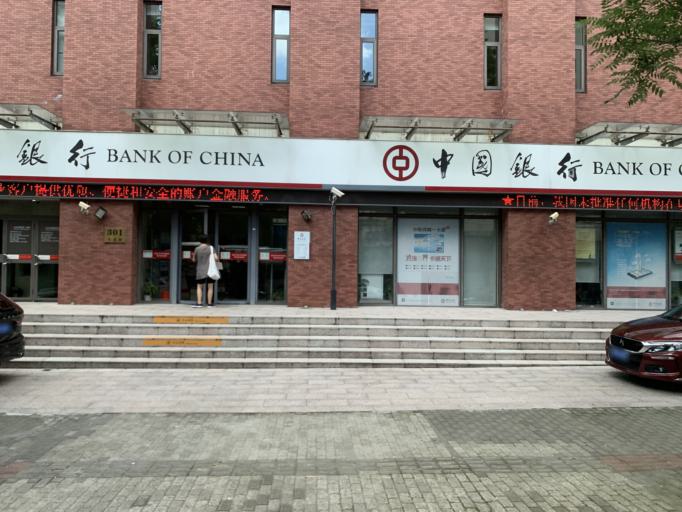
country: CN
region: Shanghai Shi
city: Huamu
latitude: 31.2033
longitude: 121.5292
